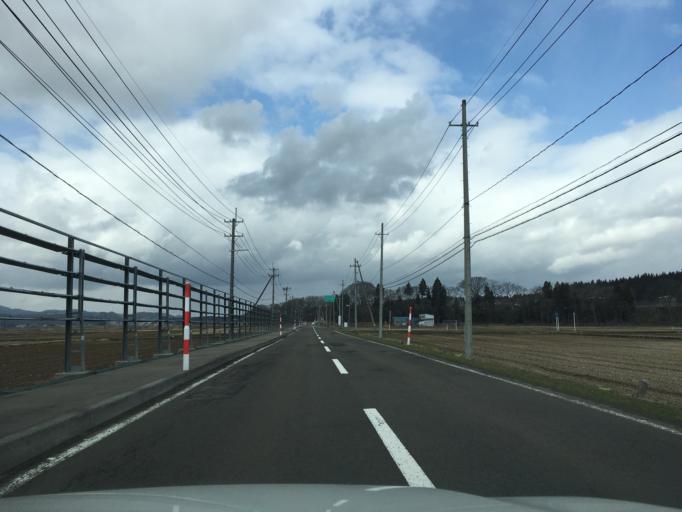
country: JP
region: Akita
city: Takanosu
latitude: 40.1397
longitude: 140.3510
